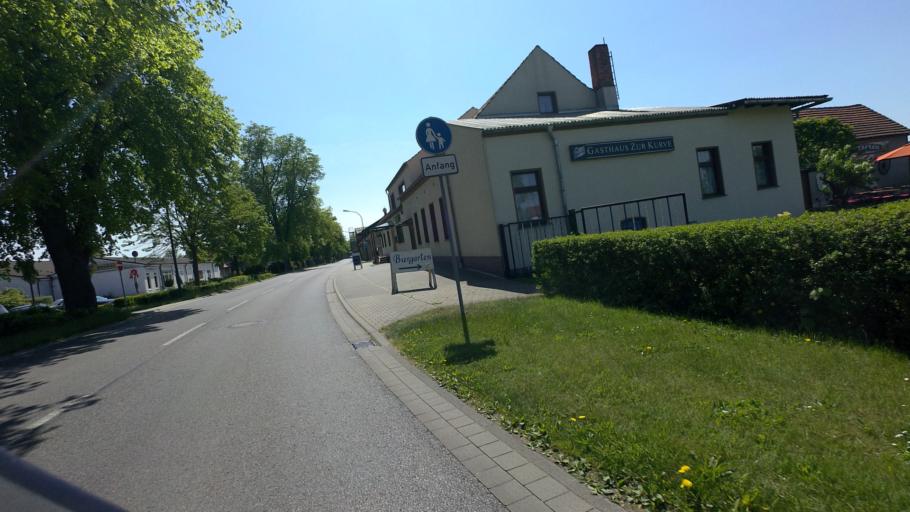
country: DE
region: Brandenburg
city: Schlepzig
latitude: 52.0794
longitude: 13.8944
